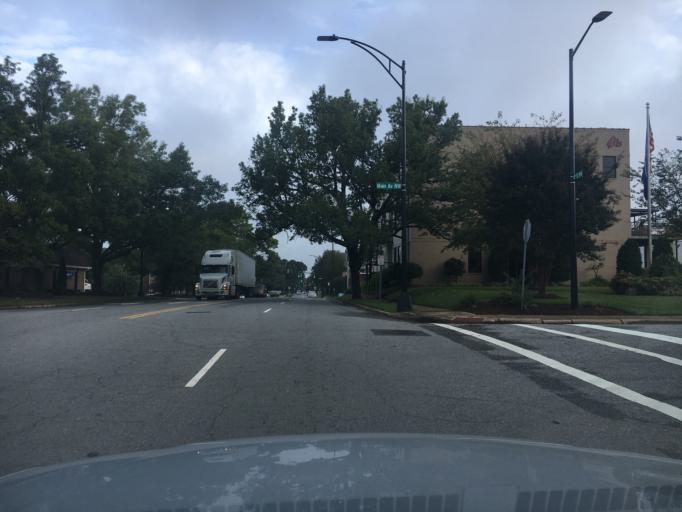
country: US
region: North Carolina
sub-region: Catawba County
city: Hickory
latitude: 35.7319
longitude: -81.3445
